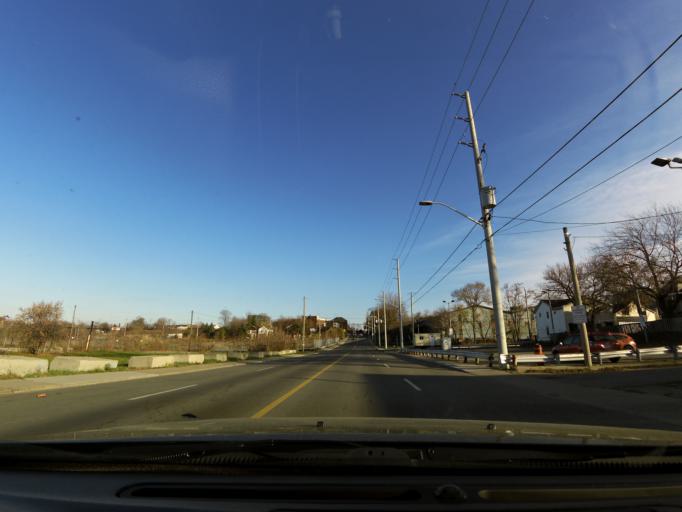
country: CA
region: Ontario
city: Hamilton
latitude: 43.2660
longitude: -79.8736
